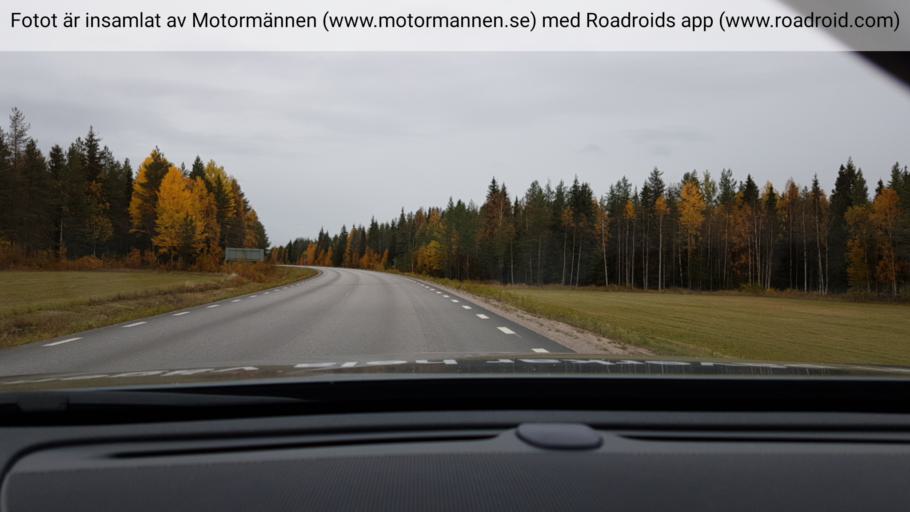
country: SE
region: Norrbotten
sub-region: Overkalix Kommun
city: OEverkalix
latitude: 66.3435
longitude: 22.8297
